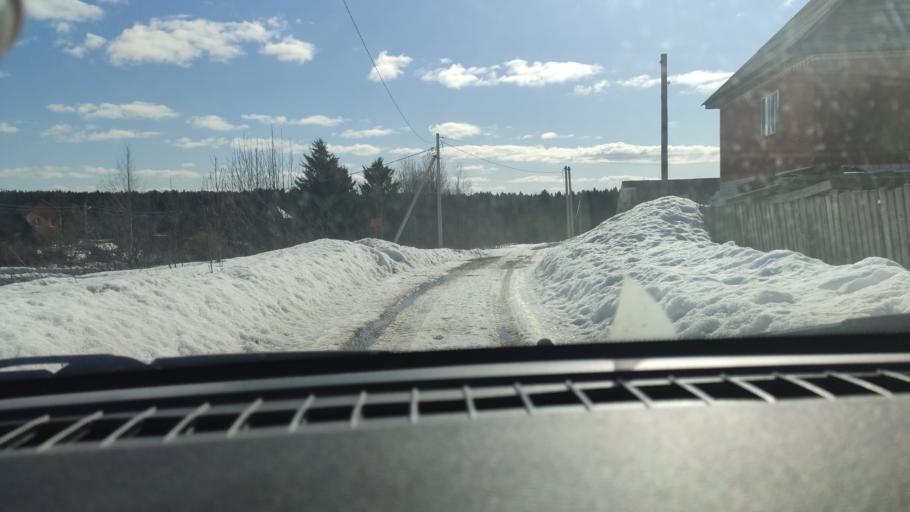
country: RU
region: Perm
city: Perm
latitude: 58.0365
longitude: 56.3984
